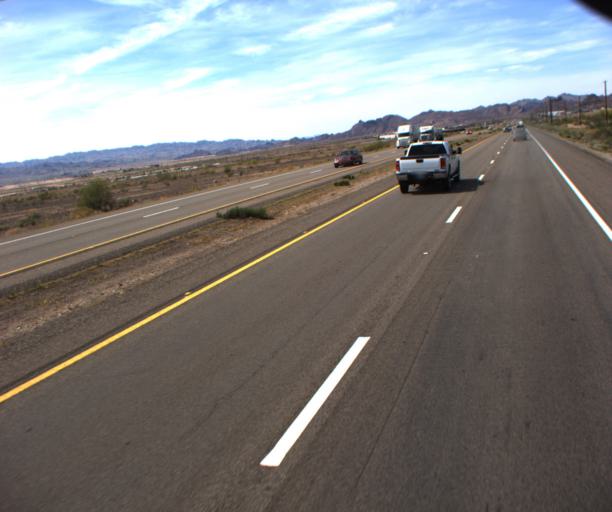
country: US
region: Arizona
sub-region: Mohave County
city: Desert Hills
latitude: 34.5498
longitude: -114.3563
